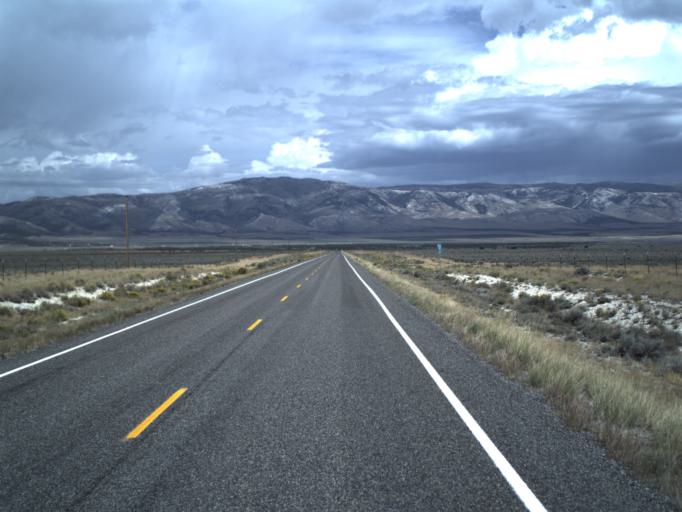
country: US
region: Idaho
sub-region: Cassia County
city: Burley
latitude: 41.7492
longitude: -113.5164
